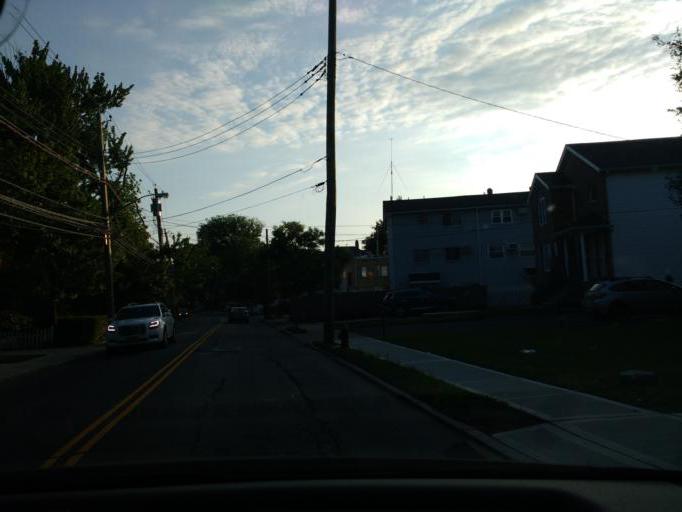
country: US
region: New York
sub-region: Richmond County
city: Staten Island
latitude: 40.5488
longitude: -74.1545
